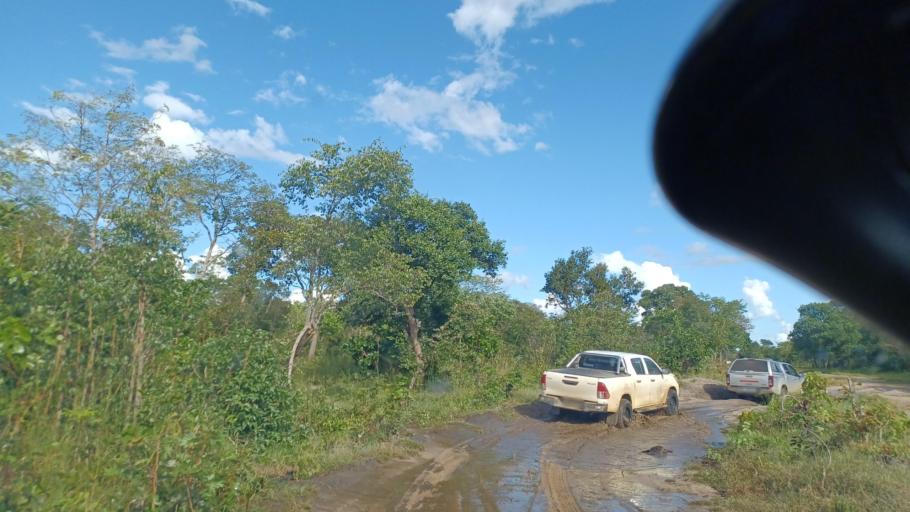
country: ZM
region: North-Western
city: Kabompo
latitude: -13.3925
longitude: 24.3102
